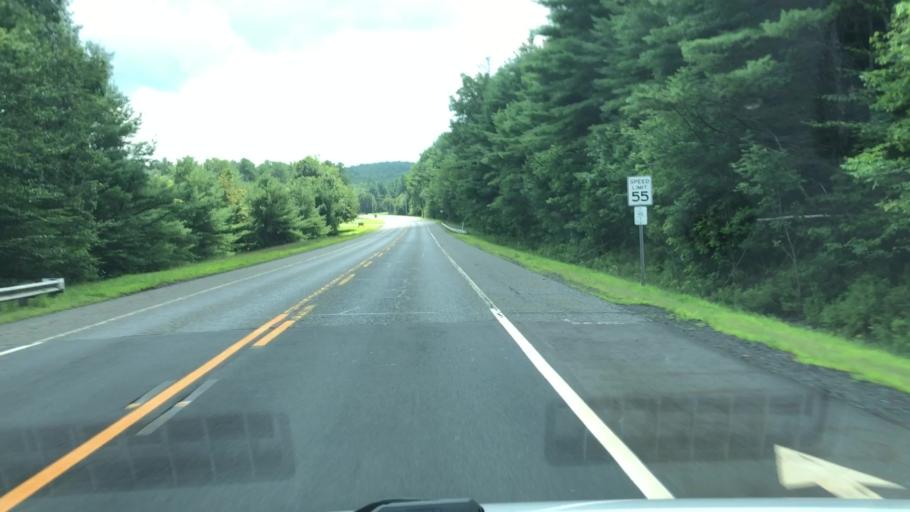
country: US
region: Massachusetts
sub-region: Franklin County
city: Ashfield
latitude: 42.4733
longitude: -72.8100
